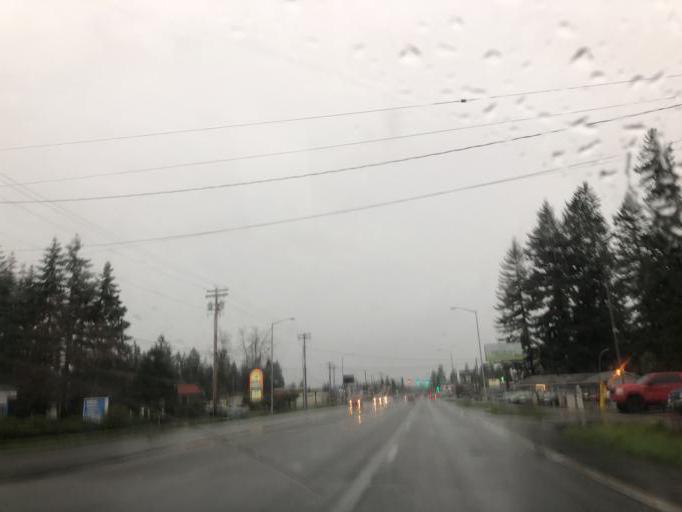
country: US
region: Washington
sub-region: Thurston County
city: Tanglewilde-Thompson Place
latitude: 47.0538
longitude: -122.7799
